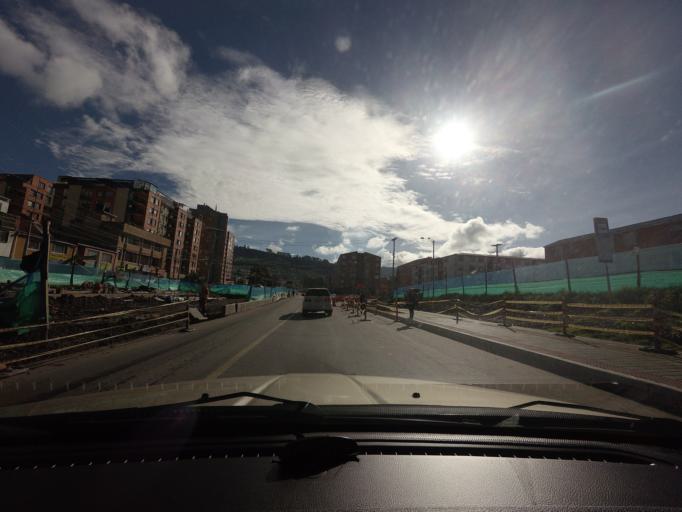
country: CO
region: Cundinamarca
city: Cota
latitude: 4.7602
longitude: -74.0392
